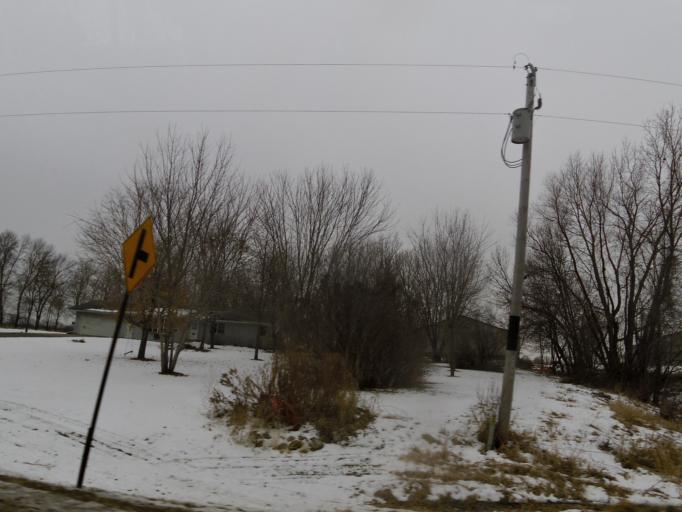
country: US
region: Minnesota
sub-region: Scott County
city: Prior Lake
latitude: 44.6284
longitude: -93.4726
